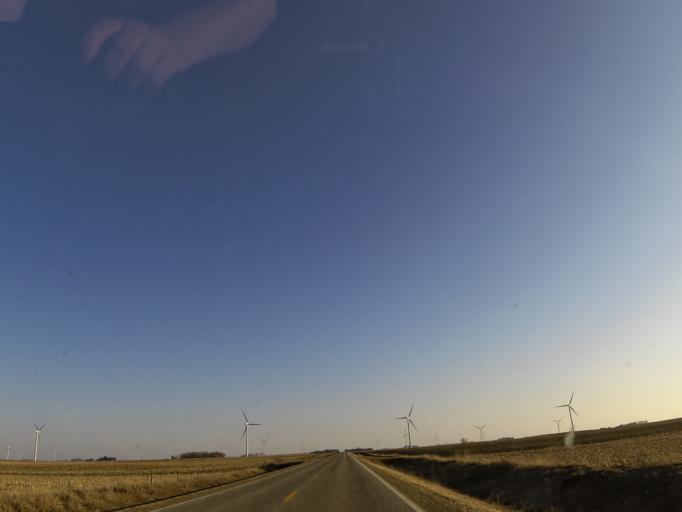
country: US
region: Iowa
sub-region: Worth County
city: Northwood
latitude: 43.4341
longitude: -93.1245
